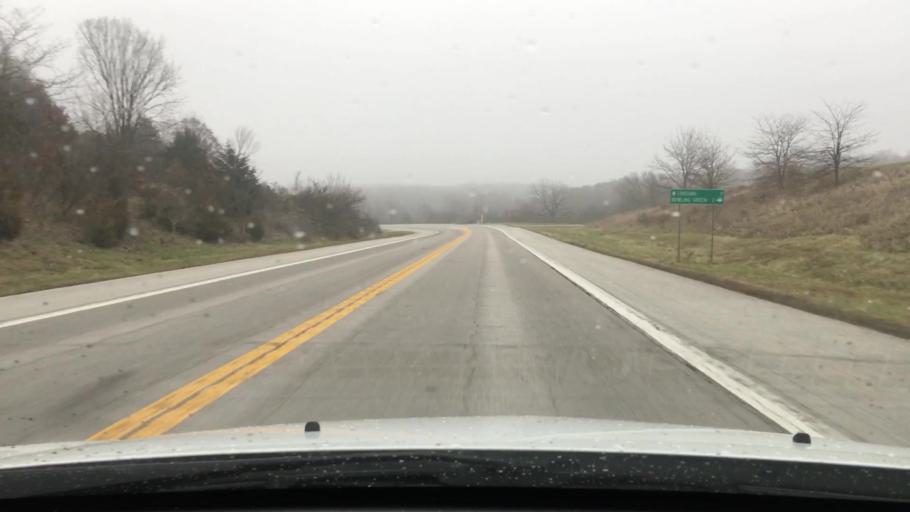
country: US
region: Missouri
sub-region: Pike County
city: Bowling Green
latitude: 39.3628
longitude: -91.1882
